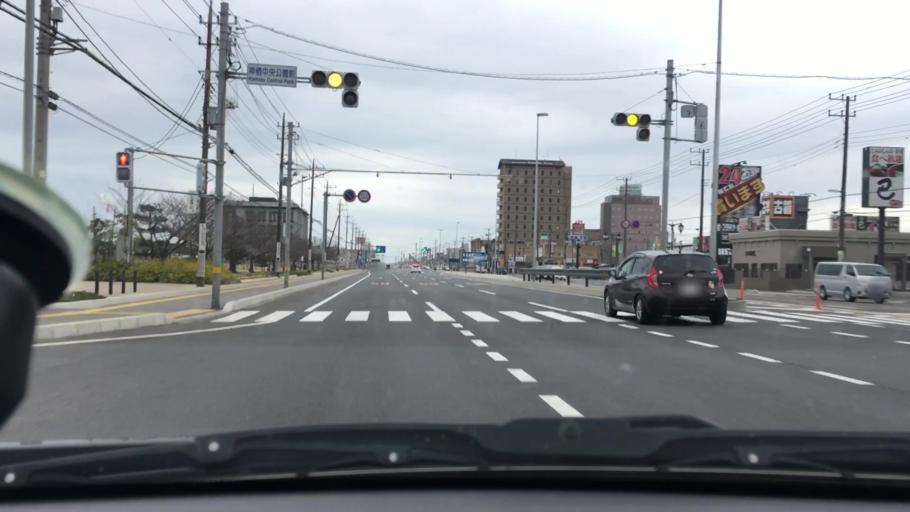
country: JP
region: Chiba
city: Omigawa
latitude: 35.8960
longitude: 140.6485
